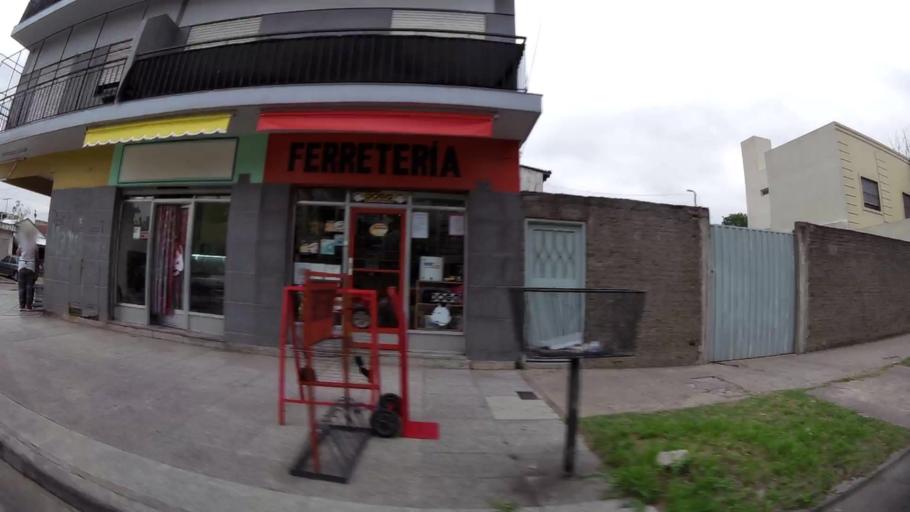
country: AR
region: Buenos Aires F.D.
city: Villa Lugano
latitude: -34.7125
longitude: -58.5175
